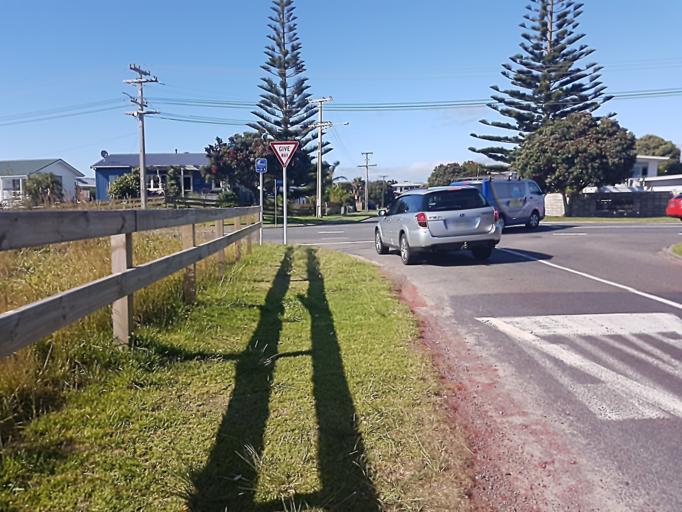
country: NZ
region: Bay of Plenty
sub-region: Tauranga City
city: Tauranga
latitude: -37.6947
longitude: 176.2795
